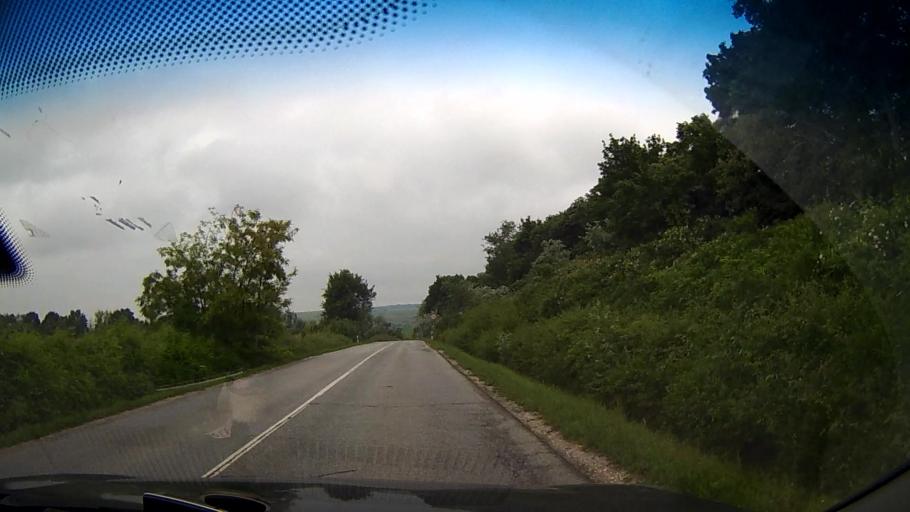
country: HU
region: Pest
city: Perbal
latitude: 47.6136
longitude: 18.7701
